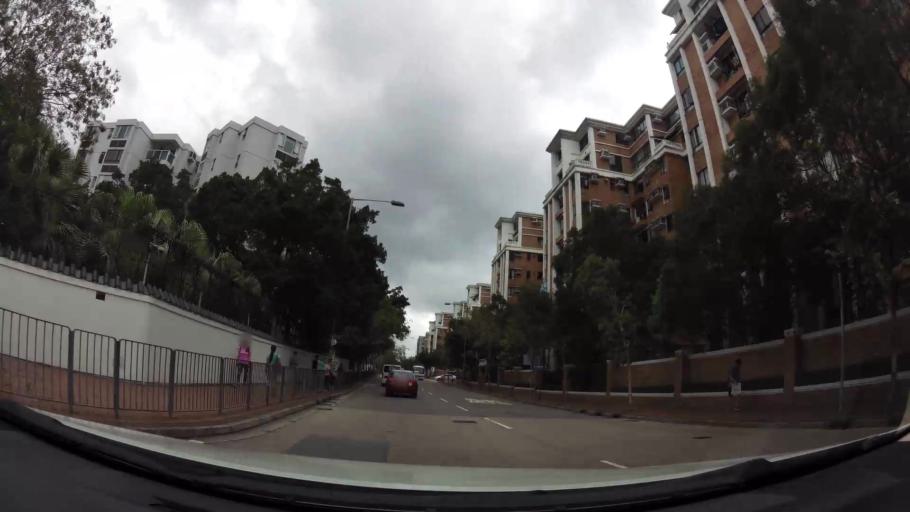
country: HK
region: Sham Shui Po
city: Sham Shui Po
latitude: 22.3349
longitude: 114.1757
